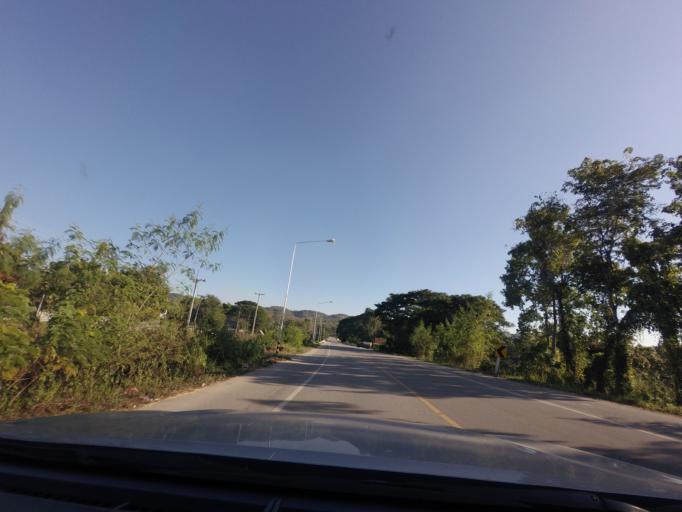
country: TH
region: Lampang
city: Chae Hom
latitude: 18.5116
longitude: 99.6440
